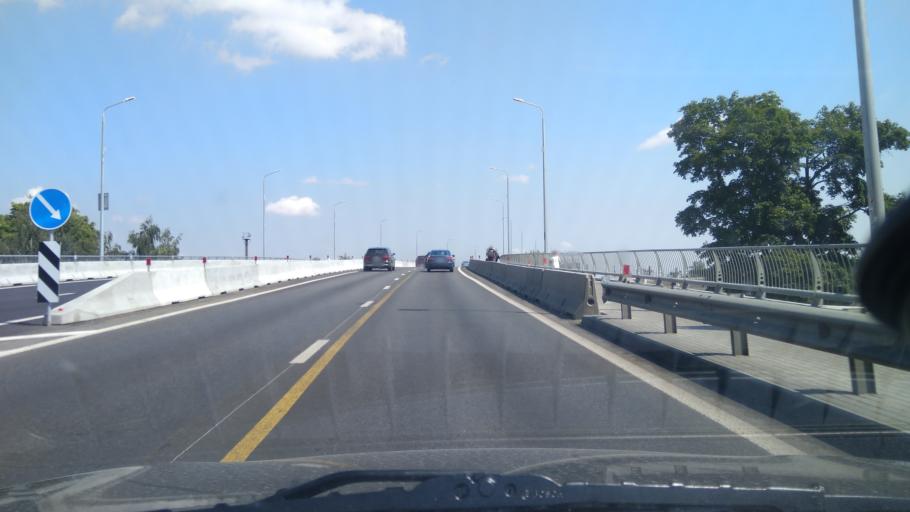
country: BY
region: Brest
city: Baranovichi
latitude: 53.1313
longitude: 26.0364
